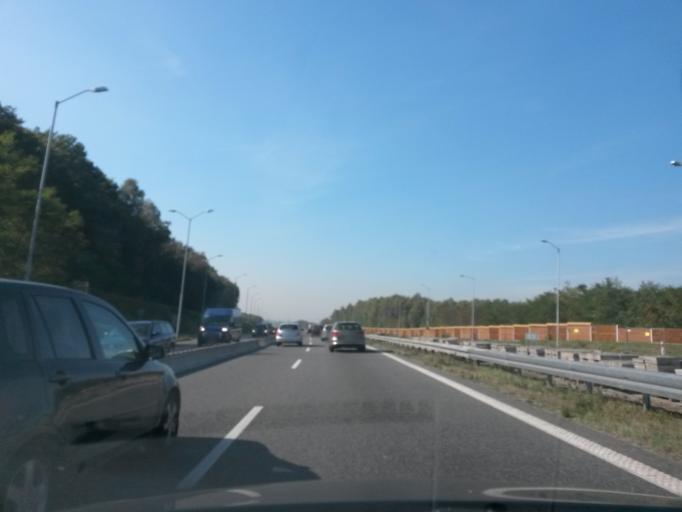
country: PL
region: Silesian Voivodeship
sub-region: Ruda Slaska
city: Ruda Slaska
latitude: 50.2523
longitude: 18.8807
